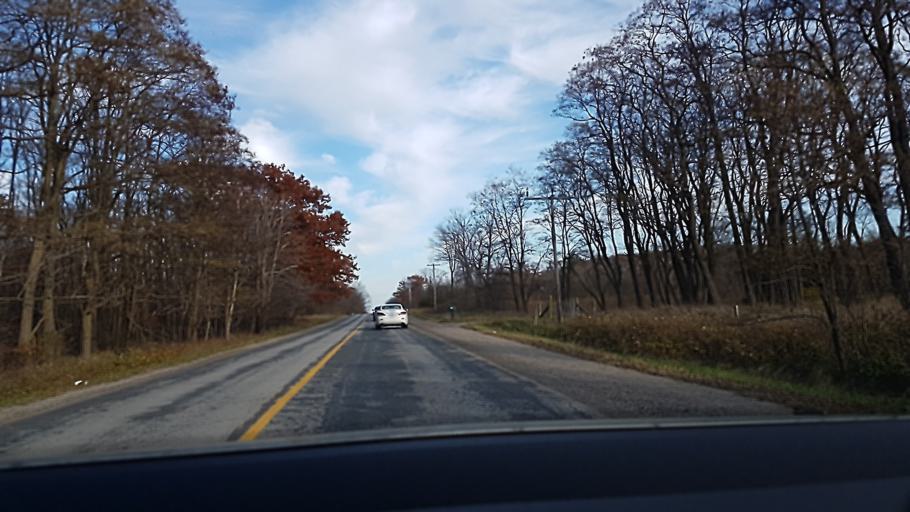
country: CA
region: Ontario
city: Barrie
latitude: 44.3672
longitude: -79.6025
